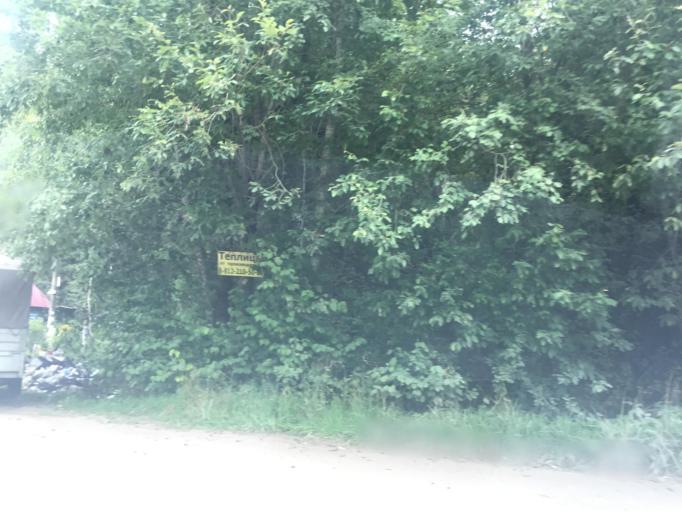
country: RU
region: Leningrad
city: Siverskiy
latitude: 59.2954
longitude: 30.0337
